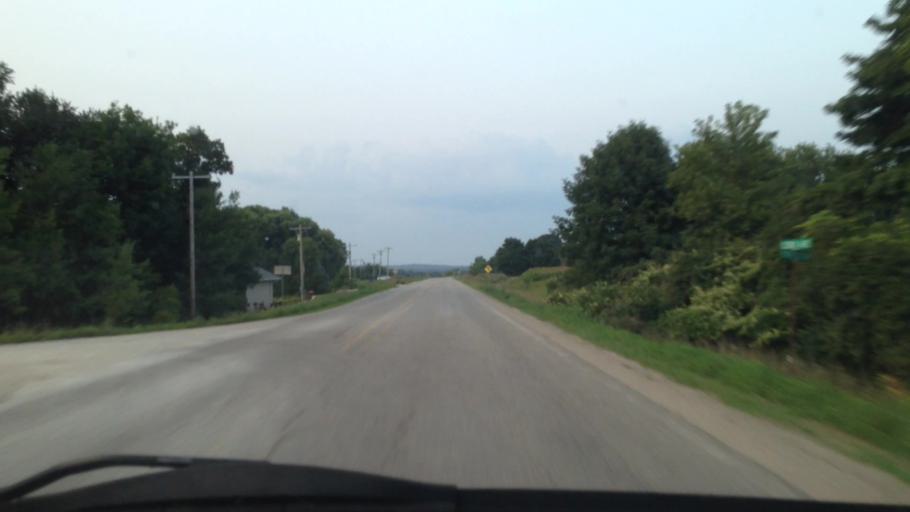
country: US
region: Iowa
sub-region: Benton County
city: Urbana
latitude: 42.1595
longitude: -91.8756
